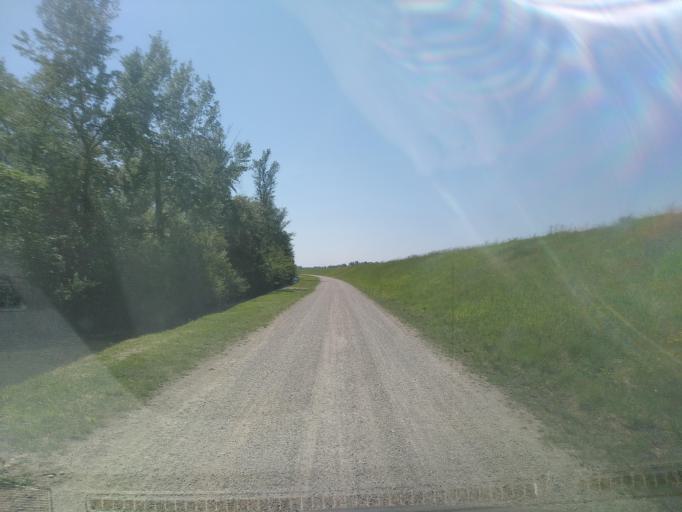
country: FR
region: Alsace
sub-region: Departement du Haut-Rhin
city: Kunheim
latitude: 48.0823
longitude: 7.5712
